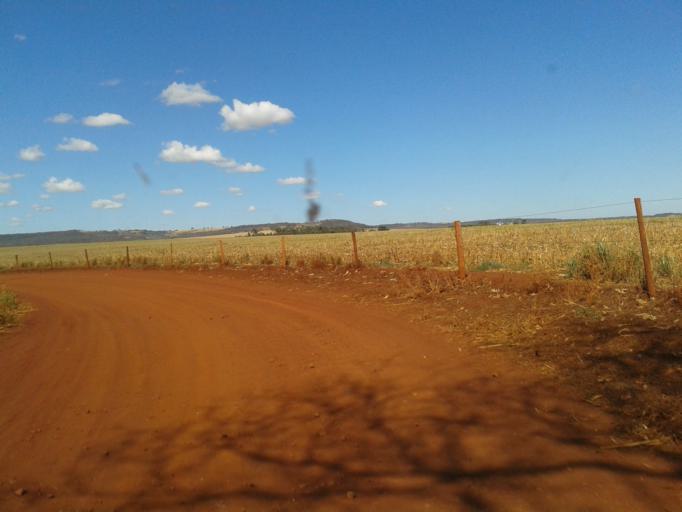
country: BR
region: Minas Gerais
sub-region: Centralina
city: Centralina
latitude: -18.5722
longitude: -49.1363
